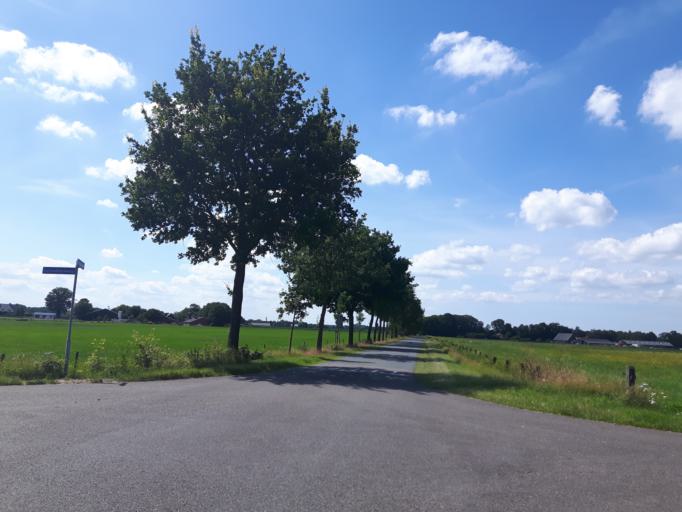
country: NL
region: Overijssel
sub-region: Gemeente Haaksbergen
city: Haaksbergen
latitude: 52.1836
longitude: 6.7446
